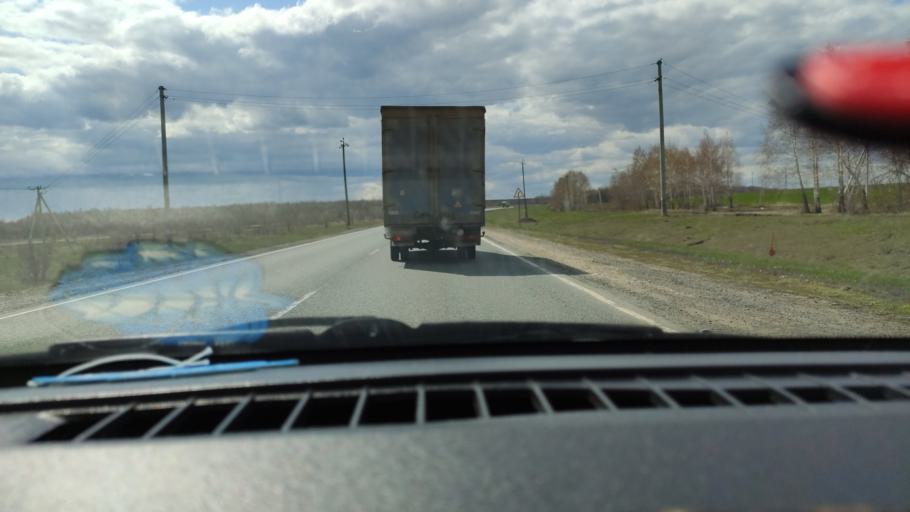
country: RU
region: Saratov
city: Balakovo
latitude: 52.1103
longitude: 47.7482
